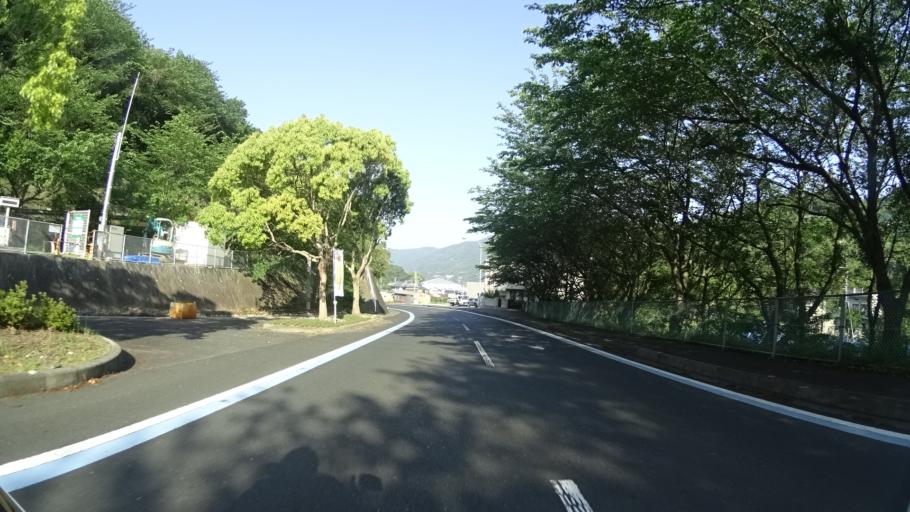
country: JP
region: Ehime
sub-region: Nishiuwa-gun
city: Ikata-cho
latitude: 33.3868
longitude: 132.1292
